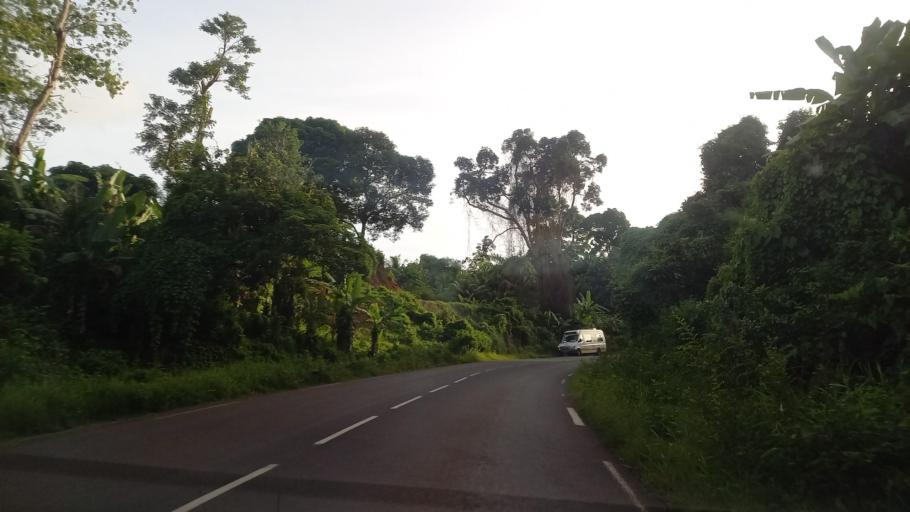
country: YT
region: Bandraboua
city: Bandraboua
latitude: -12.7420
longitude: 45.1510
